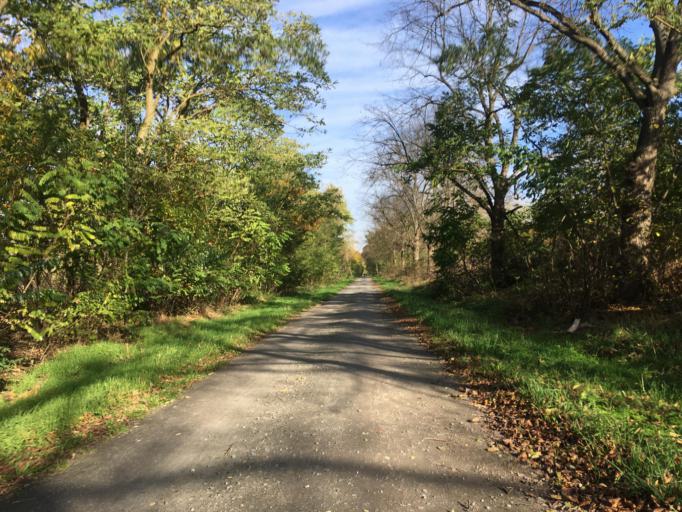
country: DE
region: Berlin
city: Buch
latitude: 52.6620
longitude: 13.4692
